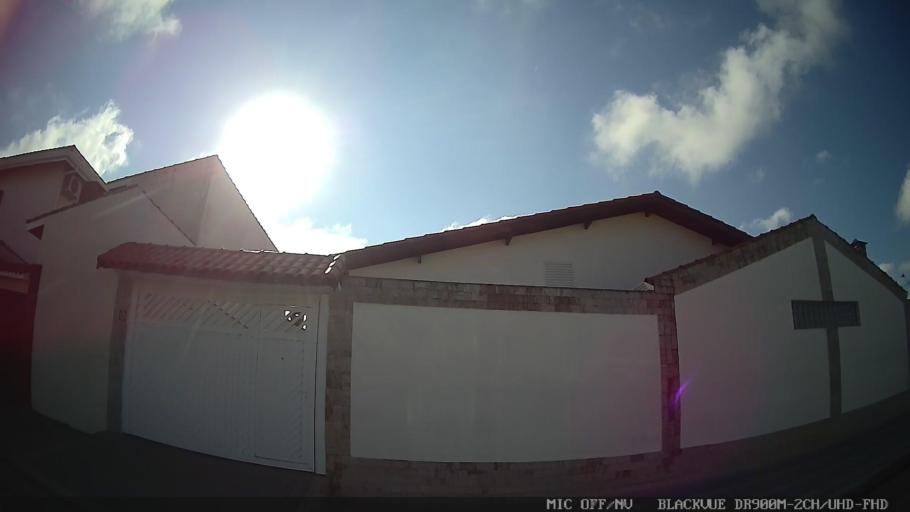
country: BR
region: Sao Paulo
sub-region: Peruibe
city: Peruibe
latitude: -24.2879
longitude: -46.9620
